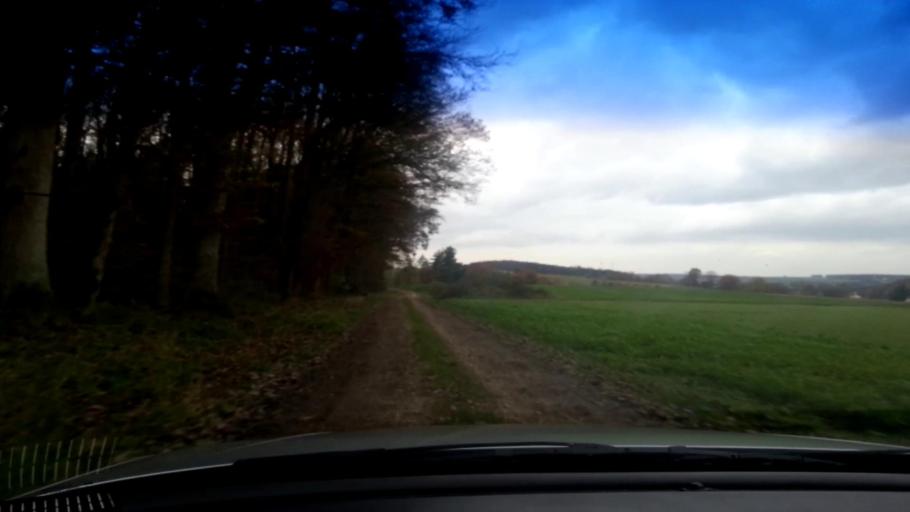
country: DE
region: Bavaria
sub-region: Upper Franconia
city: Walsdorf
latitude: 49.8583
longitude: 10.8022
